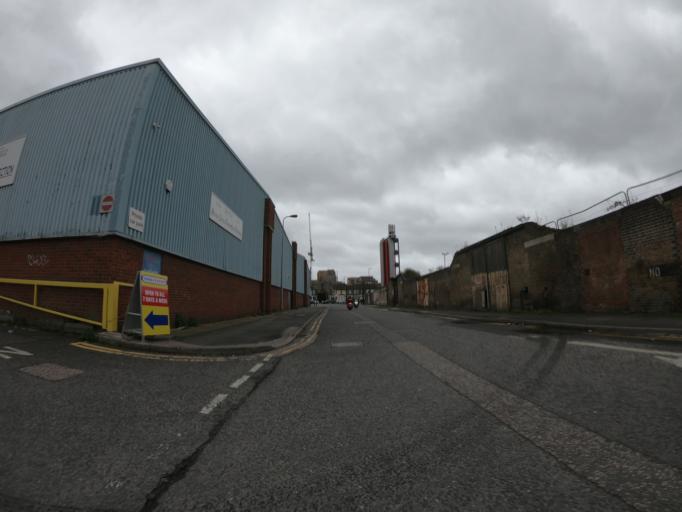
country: GB
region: England
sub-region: Greater London
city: Blackheath
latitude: 51.4878
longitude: 0.0229
